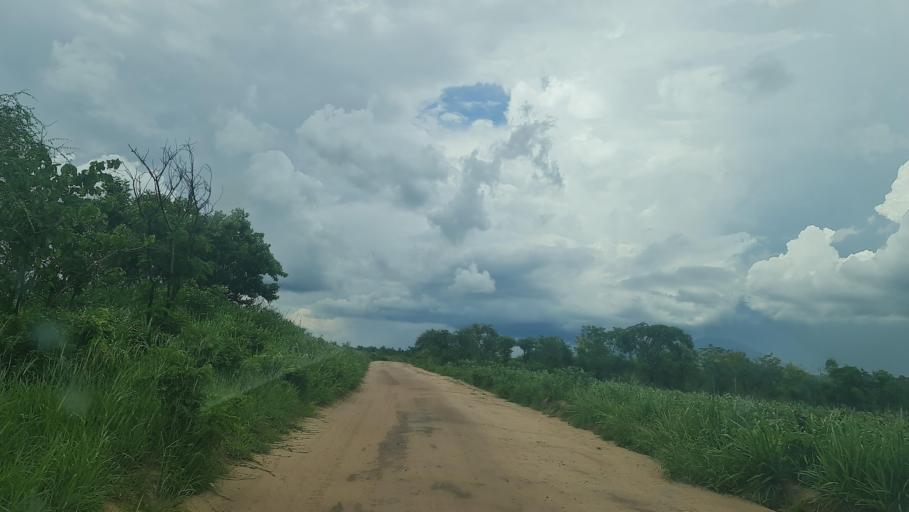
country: MW
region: Southern Region
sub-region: Nsanje District
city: Nsanje
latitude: -17.5755
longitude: 35.6561
